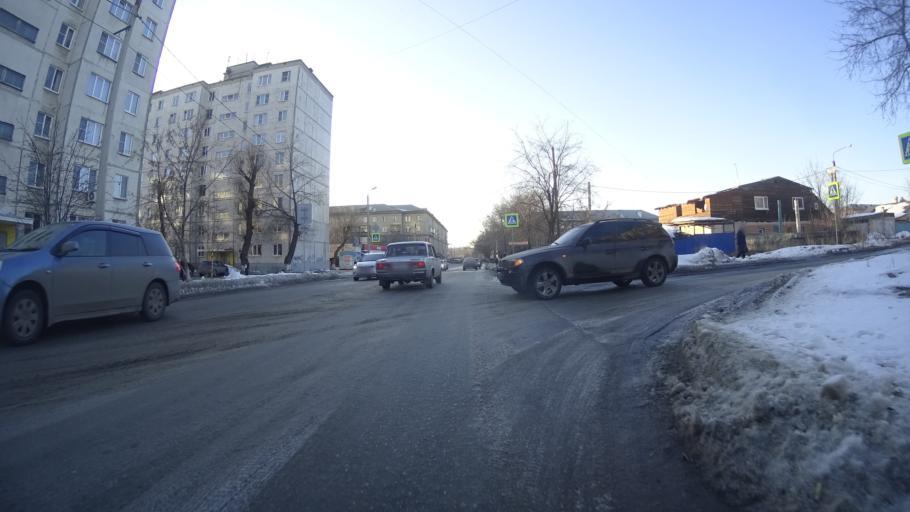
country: RU
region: Chelyabinsk
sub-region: Gorod Chelyabinsk
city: Chelyabinsk
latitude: 55.1384
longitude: 61.4448
